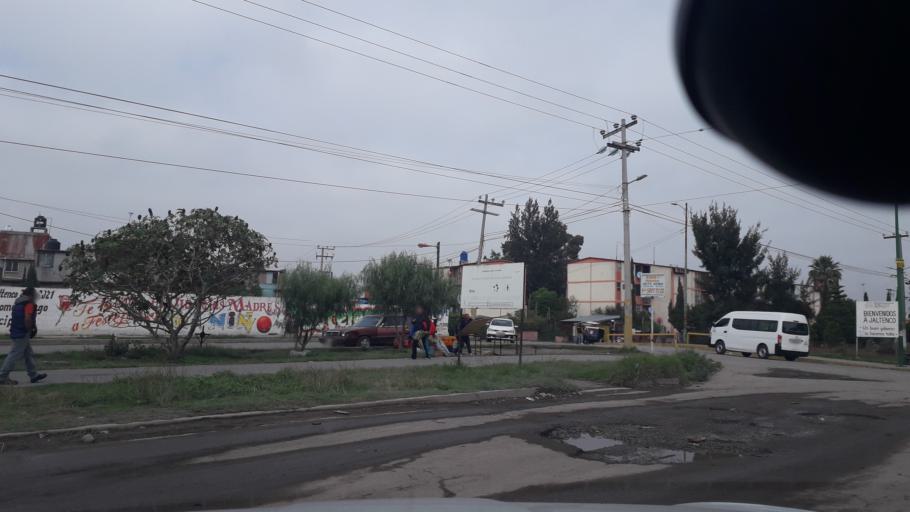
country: MX
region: Mexico
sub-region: Jaltenco
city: Alborada Jaltenco
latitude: 19.6587
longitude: -99.0693
